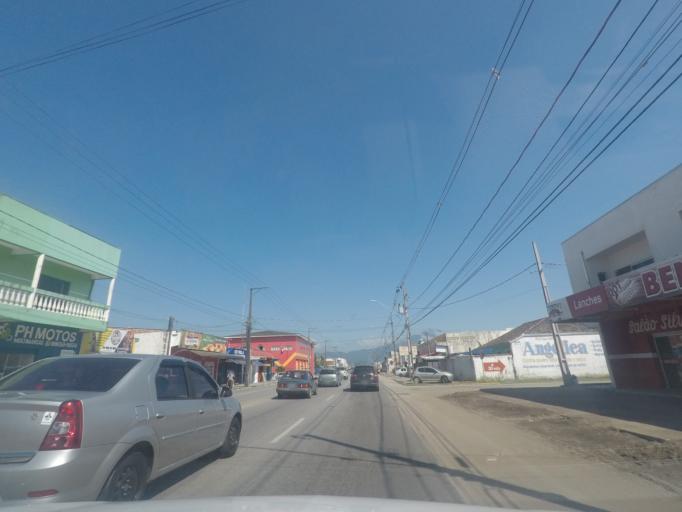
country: BR
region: Parana
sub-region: Paranagua
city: Paranagua
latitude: -25.5627
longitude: -48.5644
